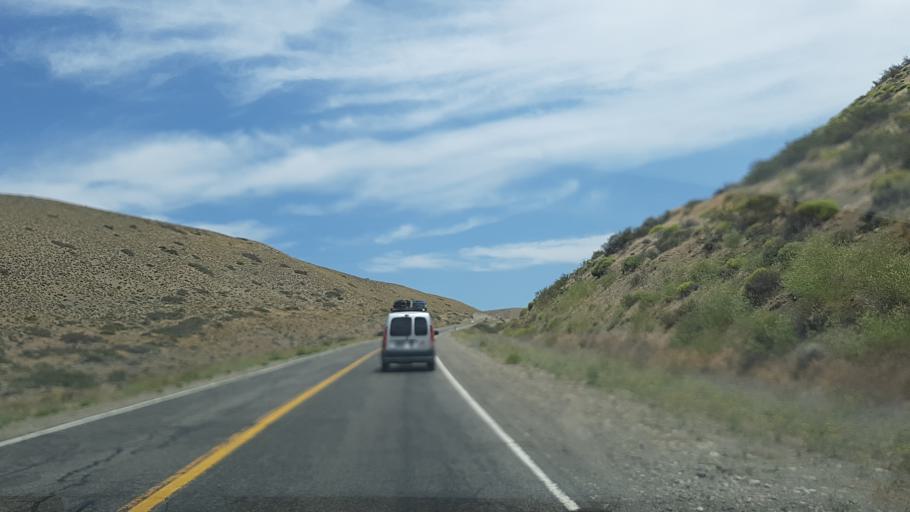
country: AR
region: Rio Negro
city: Pilcaniyeu
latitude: -40.4785
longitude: -70.6669
